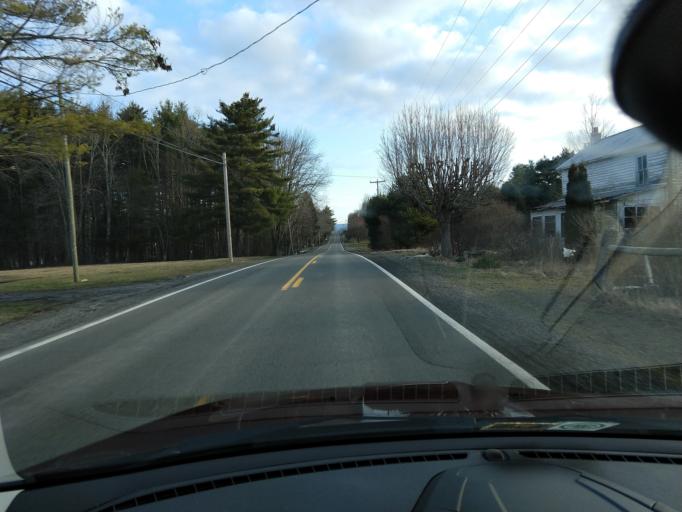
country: US
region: West Virginia
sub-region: Pocahontas County
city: Marlinton
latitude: 38.0825
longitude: -80.2816
